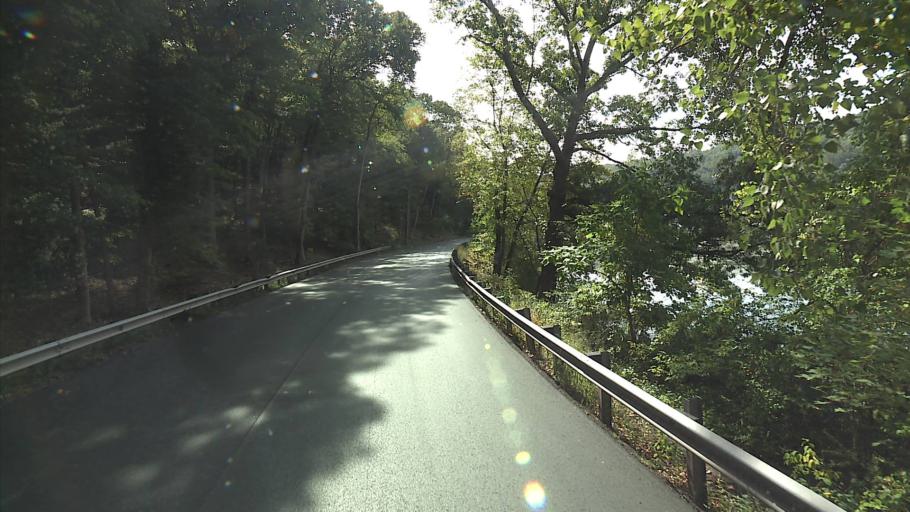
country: US
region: Connecticut
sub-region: Fairfield County
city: Shelton
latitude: 41.3375
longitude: -73.1161
